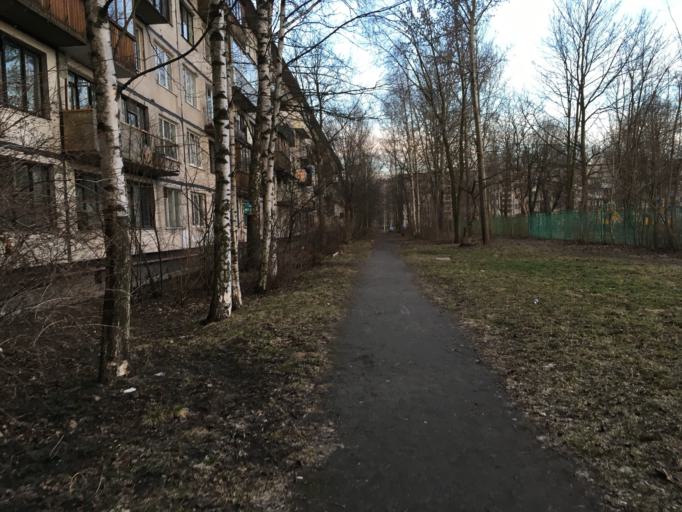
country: RU
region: St.-Petersburg
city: Obukhovo
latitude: 59.8999
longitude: 30.4668
